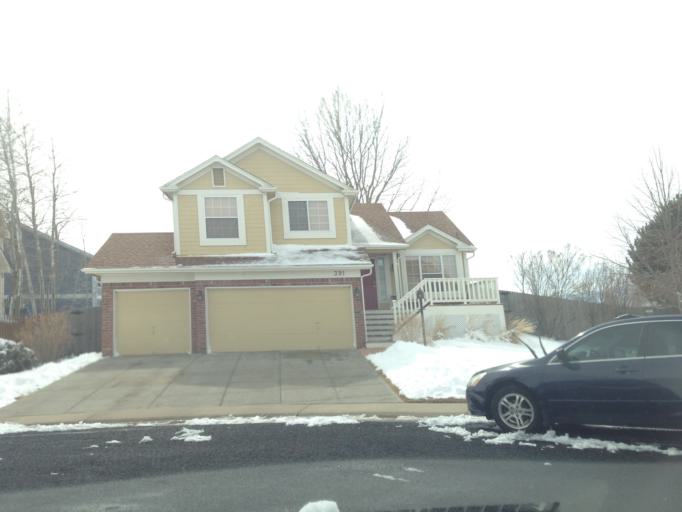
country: US
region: Colorado
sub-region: Boulder County
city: Lafayette
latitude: 39.9748
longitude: -105.0970
